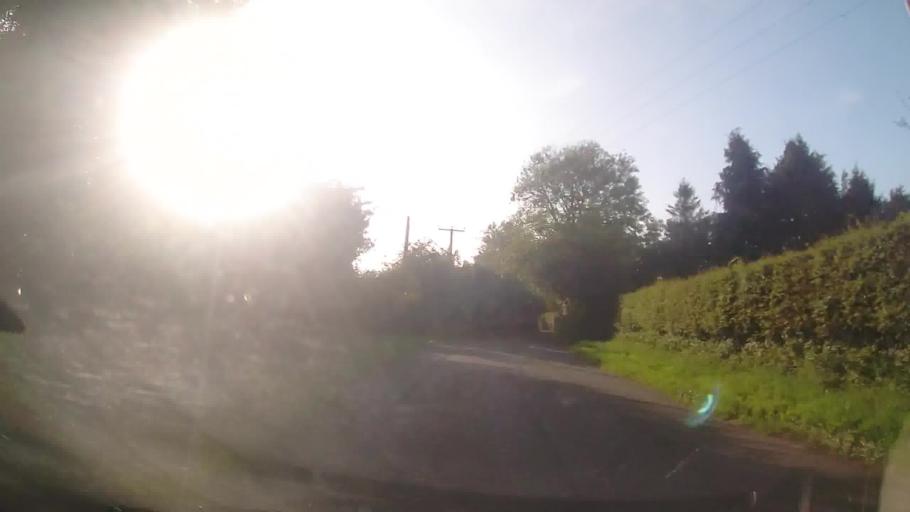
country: GB
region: Wales
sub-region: Pembrokeshire
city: Fishguard
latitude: 51.9831
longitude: -4.9496
